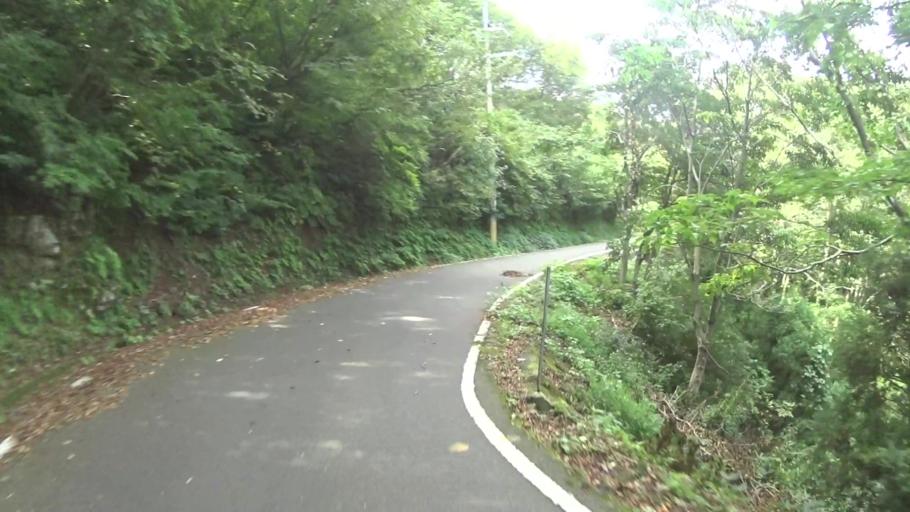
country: JP
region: Kyoto
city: Miyazu
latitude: 35.7286
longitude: 135.2003
